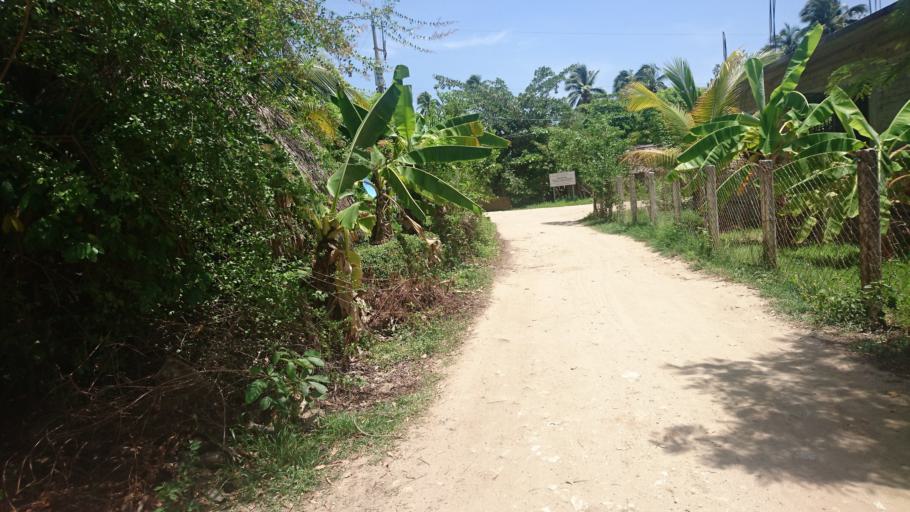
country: MX
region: Oaxaca
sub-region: Villa de Tututepec de Melchor Ocampo
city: Santa Rosa de Lima
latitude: 15.9694
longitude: -97.6799
